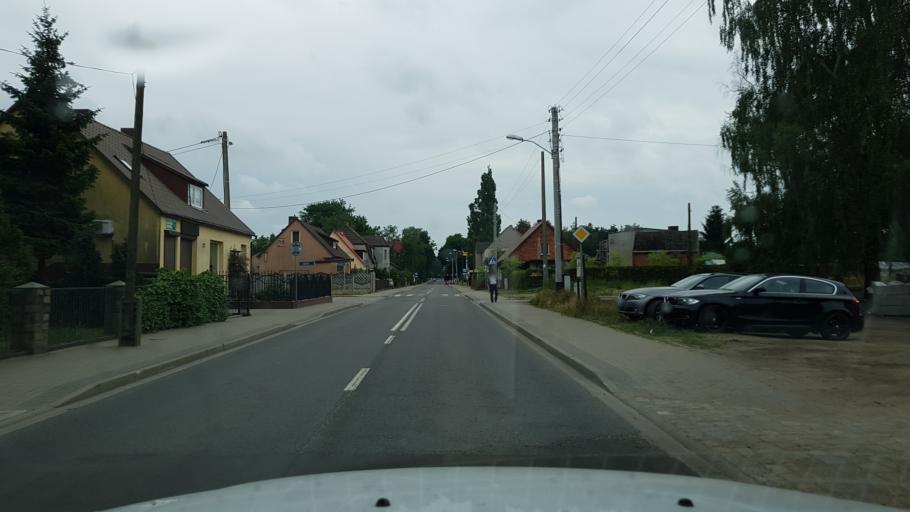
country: PL
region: West Pomeranian Voivodeship
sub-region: Powiat gryfinski
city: Stare Czarnowo
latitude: 53.3923
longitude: 14.7656
